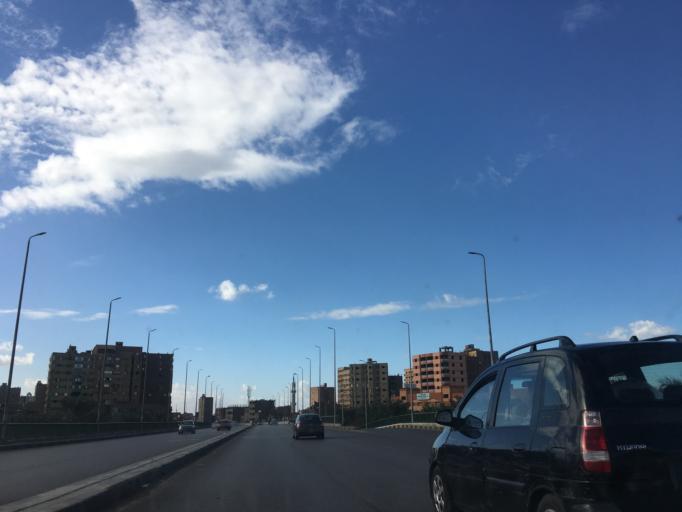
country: EG
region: Al Jizah
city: Al Jizah
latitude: 30.0297
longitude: 31.1893
